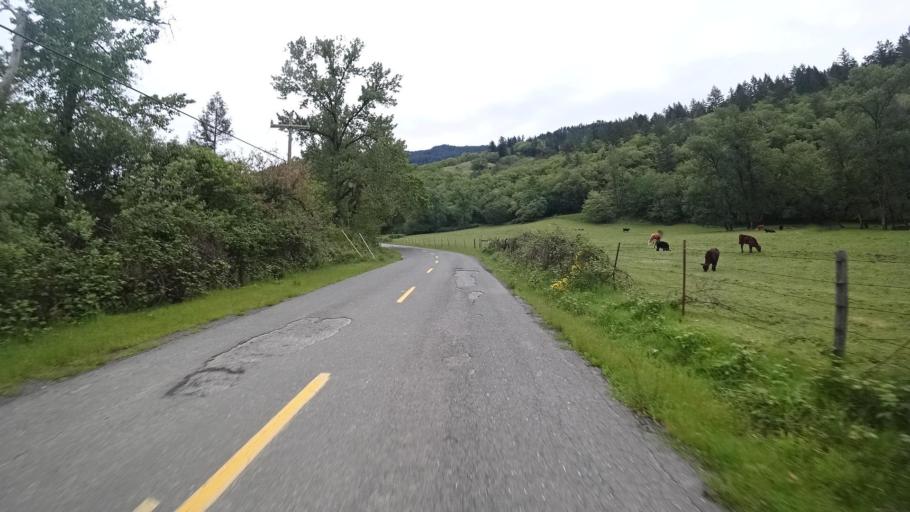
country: US
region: California
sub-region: Humboldt County
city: Blue Lake
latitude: 40.9683
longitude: -123.8413
